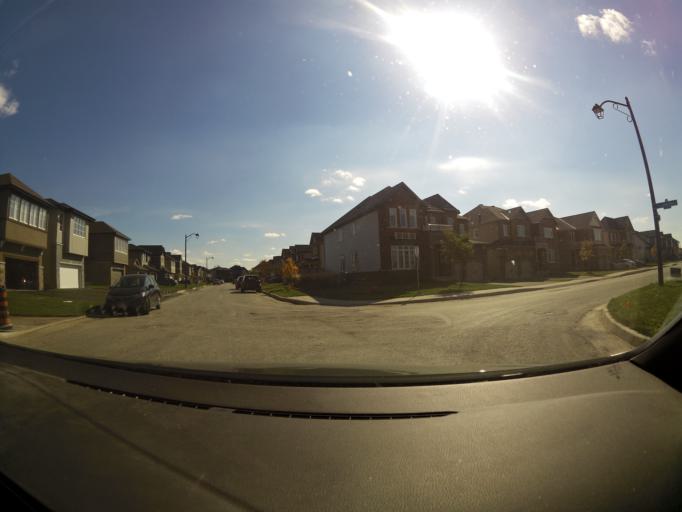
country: CA
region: Ontario
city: Bells Corners
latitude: 45.2782
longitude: -75.8803
